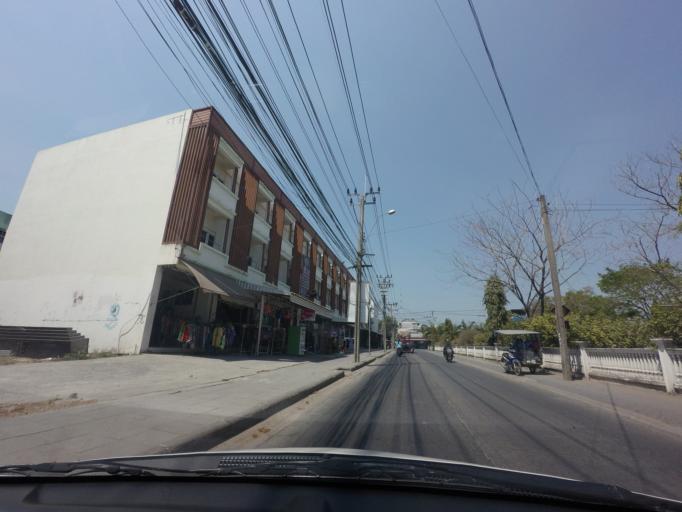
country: TH
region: Bangkok
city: Nong Chok
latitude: 13.8586
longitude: 100.8539
